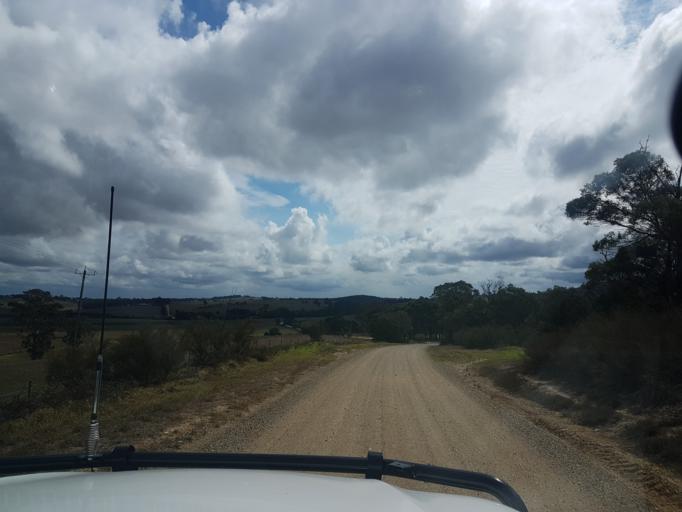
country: AU
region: Victoria
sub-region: East Gippsland
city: Bairnsdale
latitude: -37.7879
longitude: 147.5622
